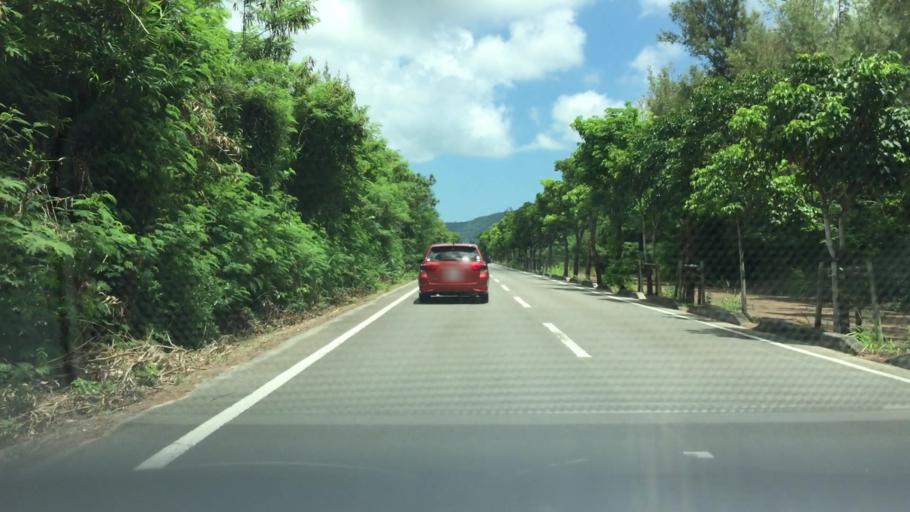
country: JP
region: Okinawa
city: Ishigaki
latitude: 24.3963
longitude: 124.1413
